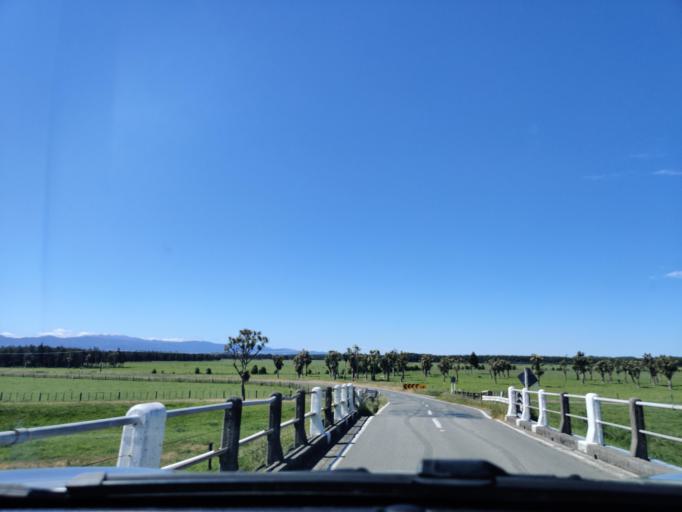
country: NZ
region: Wellington
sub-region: Upper Hutt City
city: Upper Hutt
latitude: -41.2864
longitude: 175.2688
